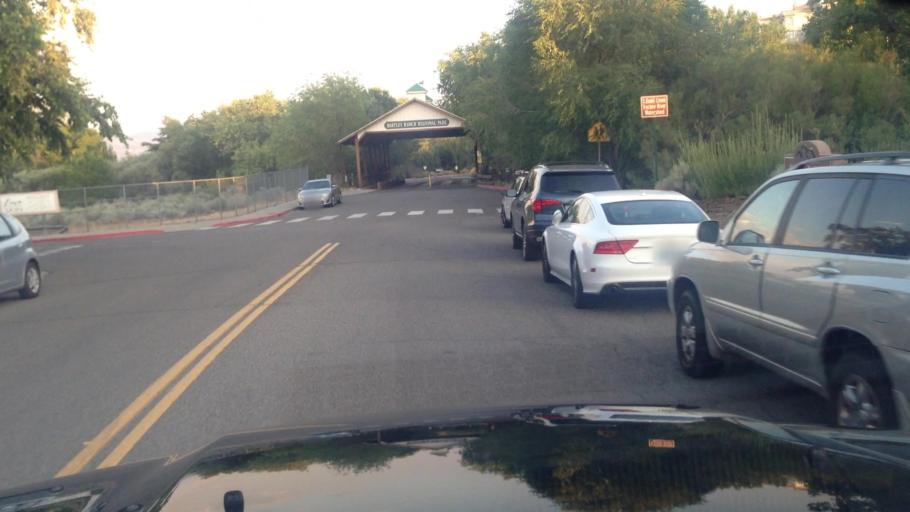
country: US
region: Nevada
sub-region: Washoe County
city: Reno
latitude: 39.4699
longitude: -119.8073
